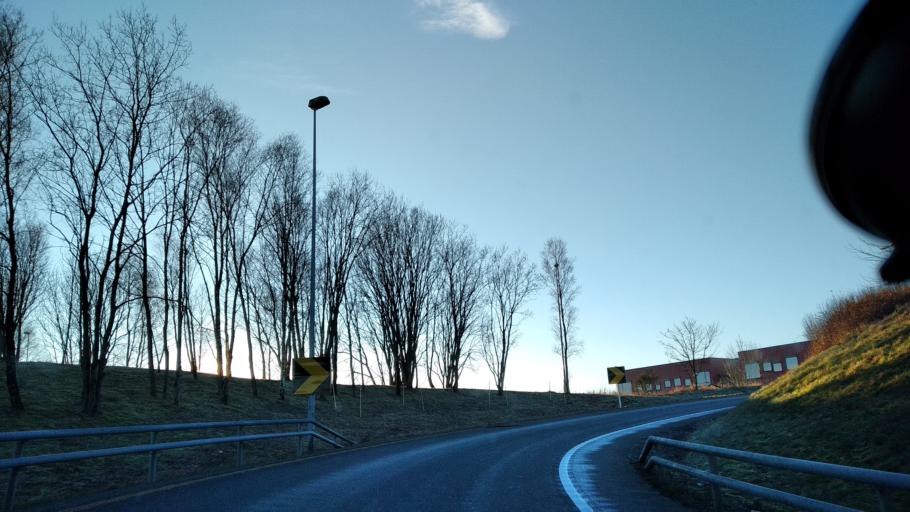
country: NO
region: Rogaland
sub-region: Sandnes
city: Sandnes
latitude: 58.8573
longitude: 5.7114
